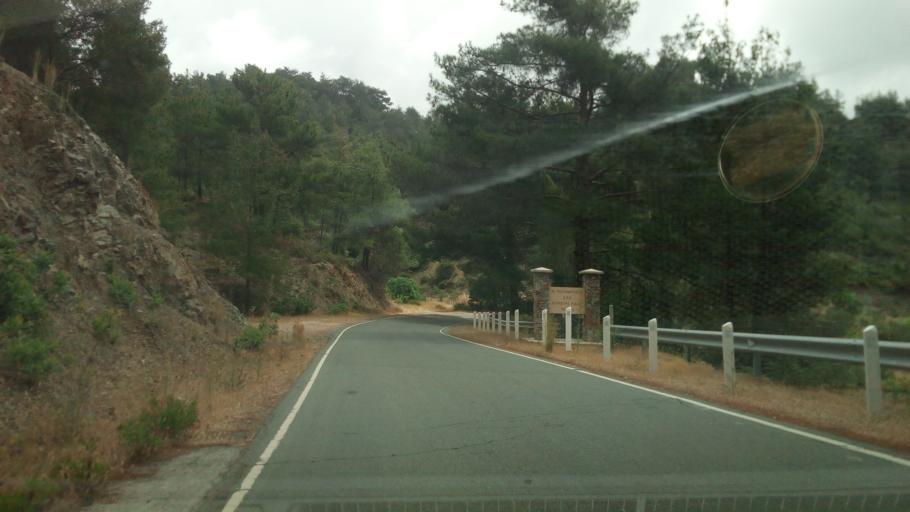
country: CY
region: Limassol
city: Pelendri
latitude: 34.8969
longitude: 32.9953
